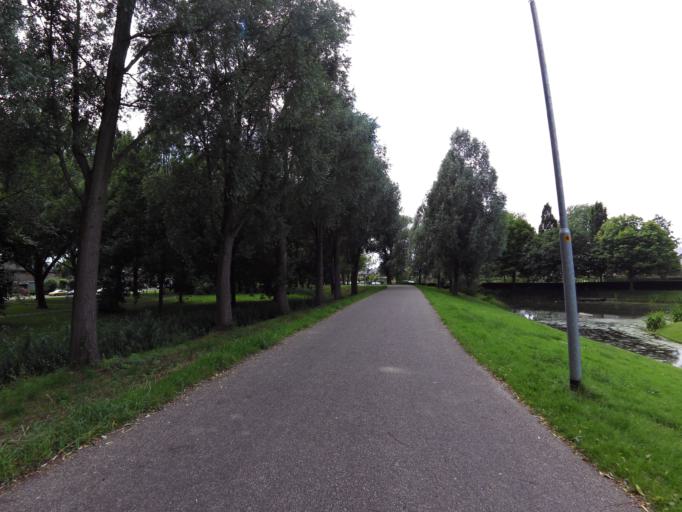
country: NL
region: South Holland
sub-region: Gemeente Dordrecht
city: Dordrecht
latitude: 51.7891
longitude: 4.7101
